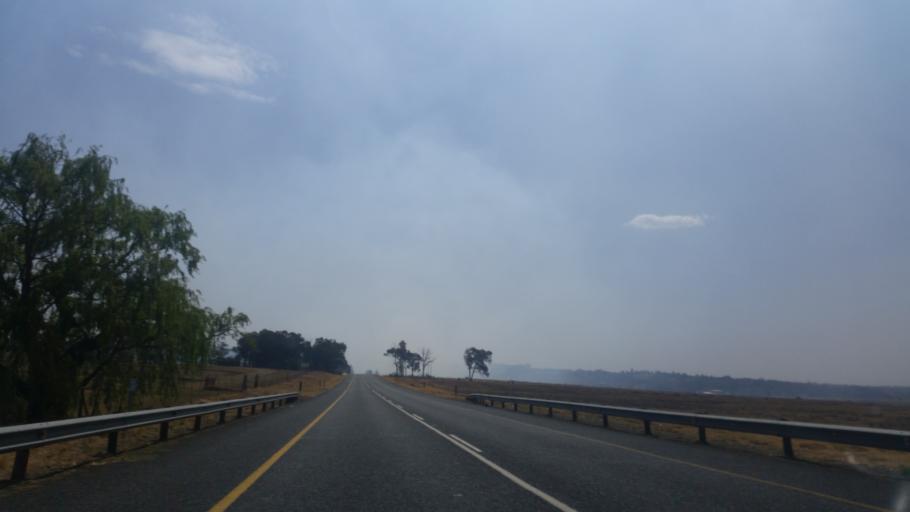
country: ZA
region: Orange Free State
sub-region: Thabo Mofutsanyana District Municipality
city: Bethlehem
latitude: -28.2716
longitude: 28.3714
